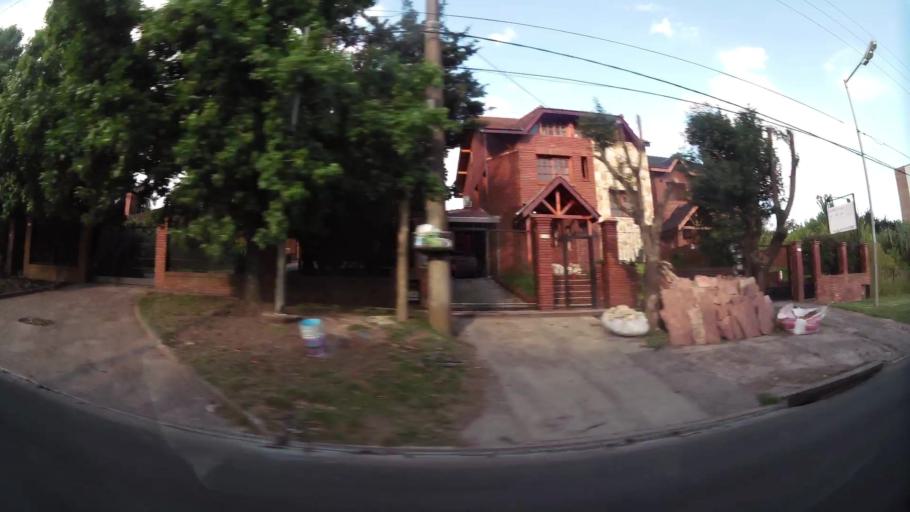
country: AR
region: Buenos Aires
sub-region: Partido de Tigre
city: Tigre
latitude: -34.4661
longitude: -58.6254
